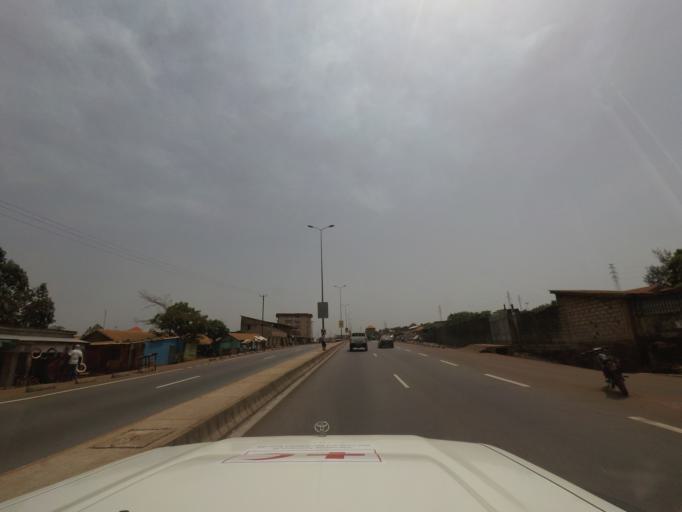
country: GN
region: Kindia
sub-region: Prefecture de Dubreka
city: Dubreka
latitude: 9.6918
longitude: -13.5088
